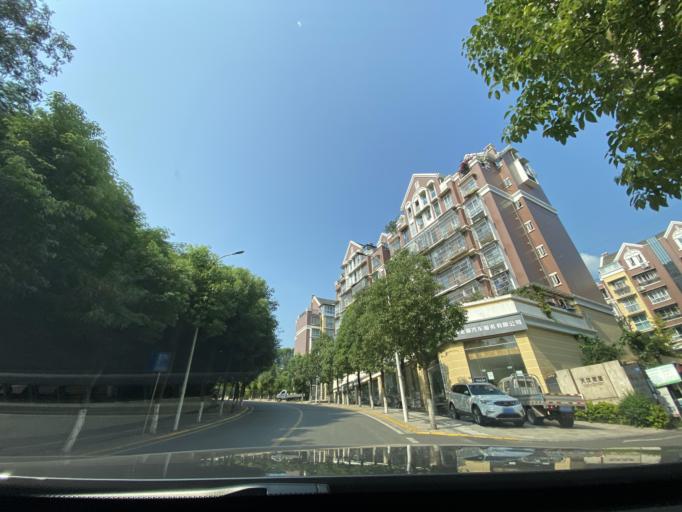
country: CN
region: Sichuan
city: Jiancheng
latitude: 30.4194
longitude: 104.5444
